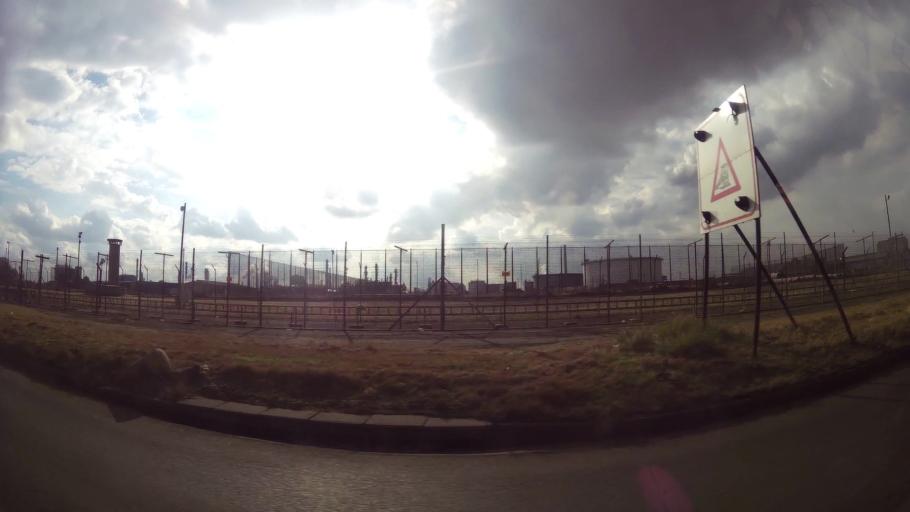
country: ZA
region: Orange Free State
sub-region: Fezile Dabi District Municipality
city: Sasolburg
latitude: -26.8344
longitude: 27.8518
